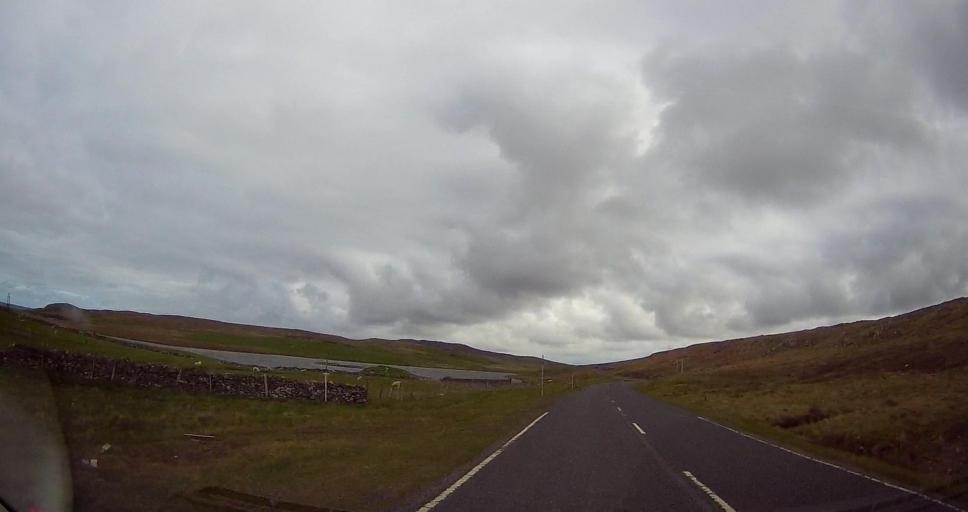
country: GB
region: Scotland
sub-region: Shetland Islands
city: Shetland
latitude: 60.6882
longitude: -0.9625
